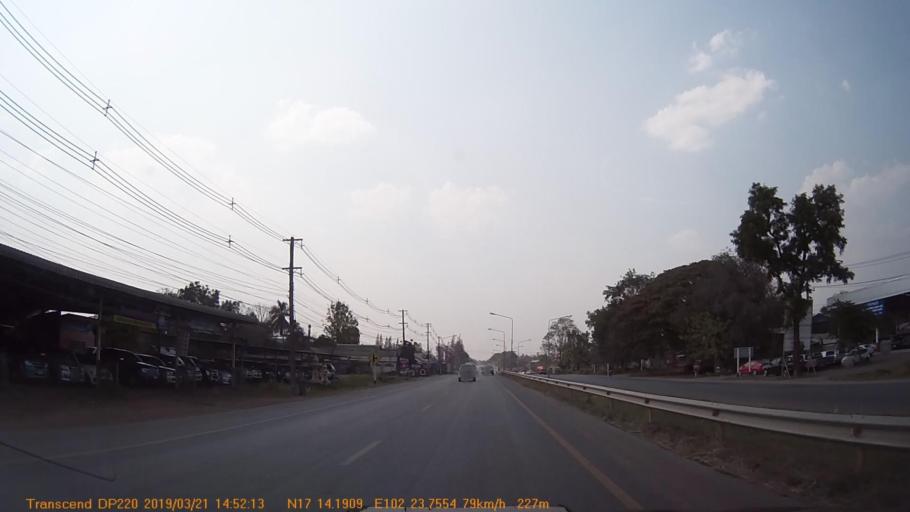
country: TH
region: Changwat Nong Bua Lamphu
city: Nong Bua Lamphu
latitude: 17.2368
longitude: 102.3957
